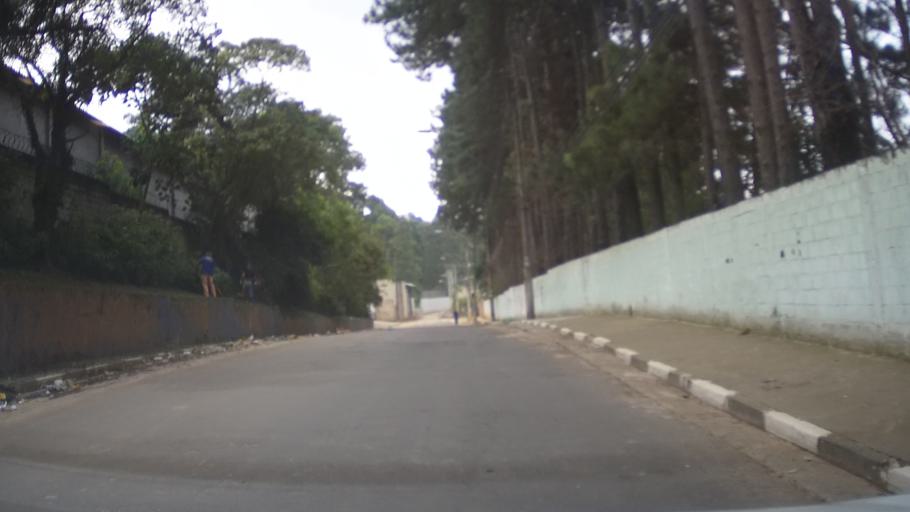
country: BR
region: Sao Paulo
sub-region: Guarulhos
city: Guarulhos
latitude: -23.4235
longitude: -46.5126
